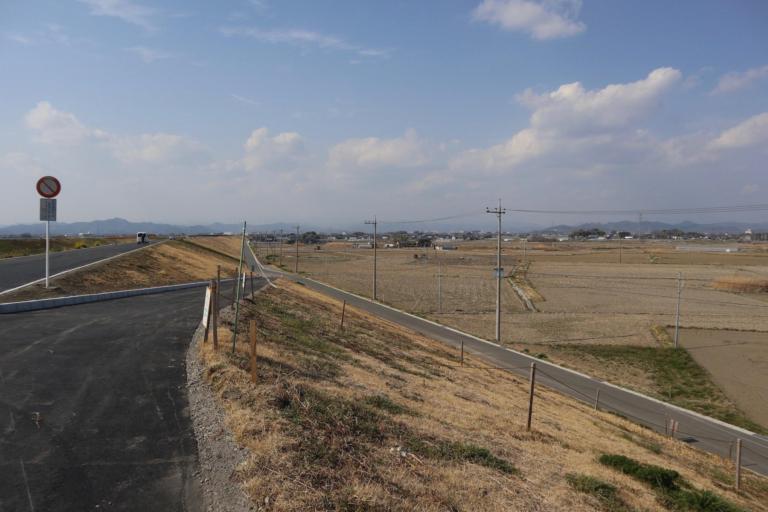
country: JP
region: Tochigi
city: Sano
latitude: 36.2719
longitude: 139.5848
